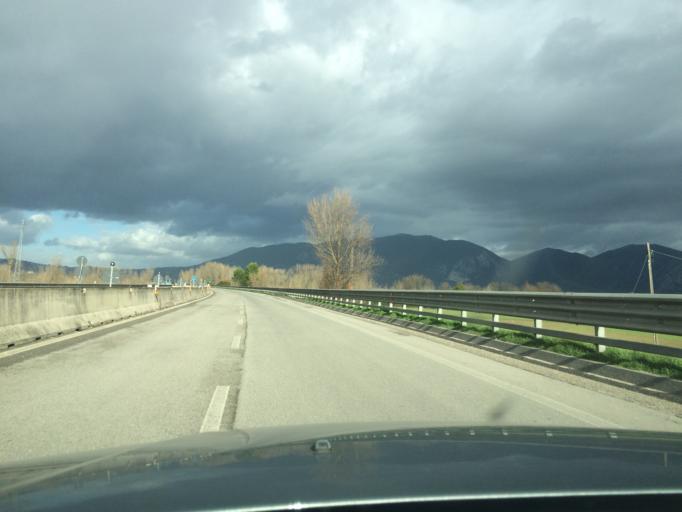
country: IT
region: Umbria
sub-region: Provincia di Terni
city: Terni
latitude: 42.5537
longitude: 12.5839
